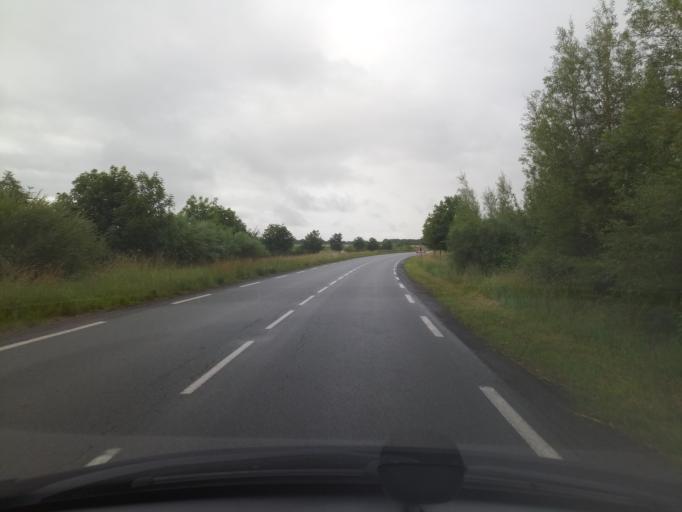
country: FR
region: Poitou-Charentes
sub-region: Departement de la Charente-Maritime
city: Courcon
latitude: 46.1893
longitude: -0.8558
